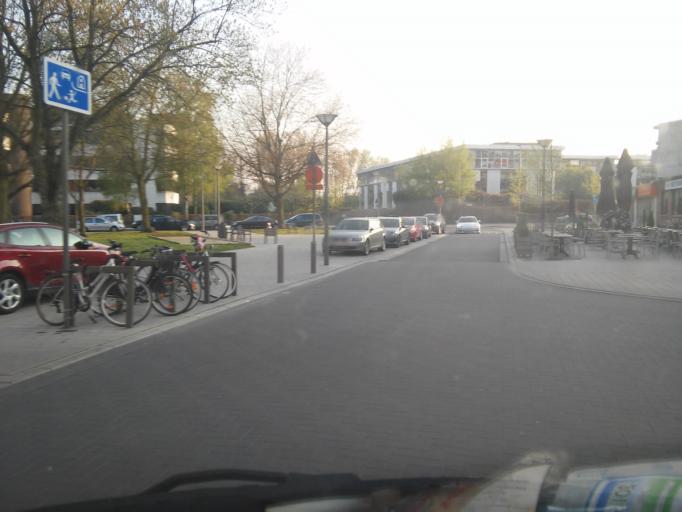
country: BE
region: Flanders
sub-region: Provincie Antwerpen
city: Aartselaar
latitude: 51.1750
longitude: 4.4026
